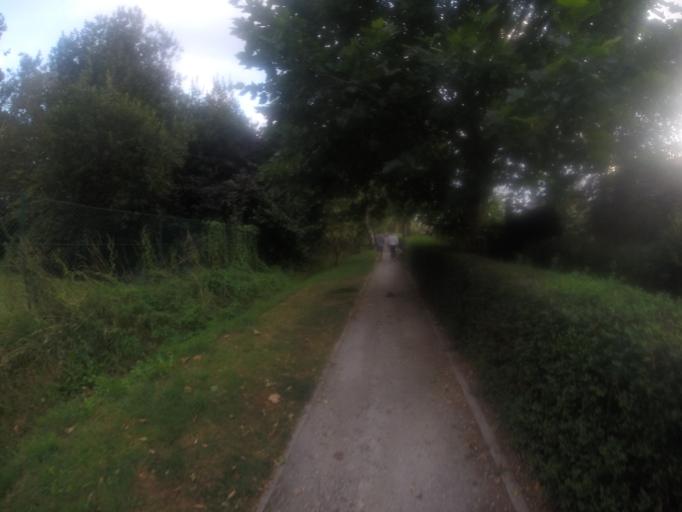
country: BE
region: Flanders
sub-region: Provincie West-Vlaanderen
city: Poperinge
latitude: 50.8590
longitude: 2.7176
